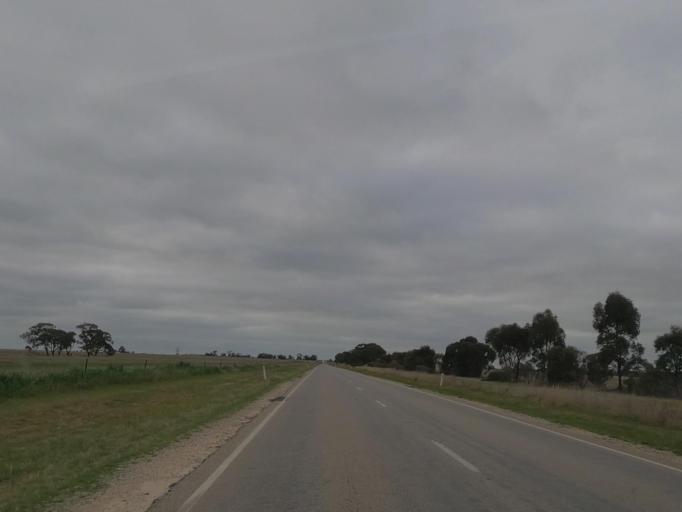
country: AU
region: Victoria
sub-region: Greater Bendigo
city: Long Gully
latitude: -36.5407
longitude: 143.9412
